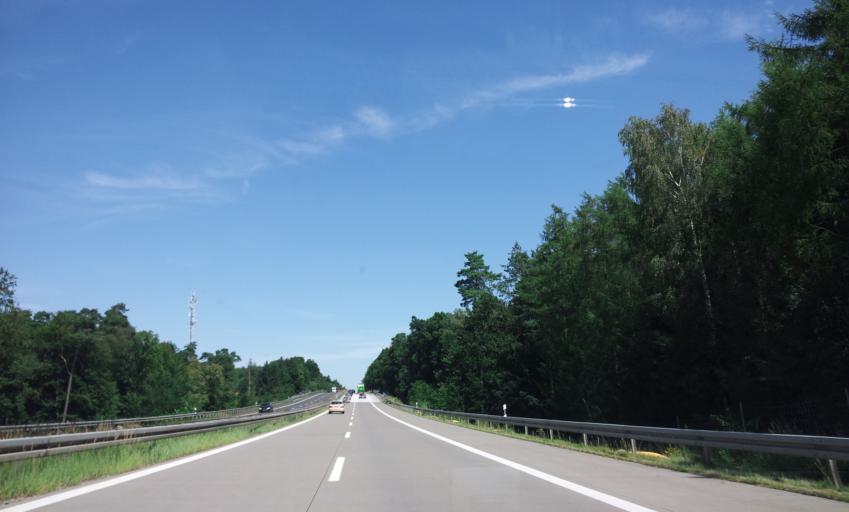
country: DE
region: Brandenburg
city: Althuttendorf
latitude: 53.0190
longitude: 13.8280
